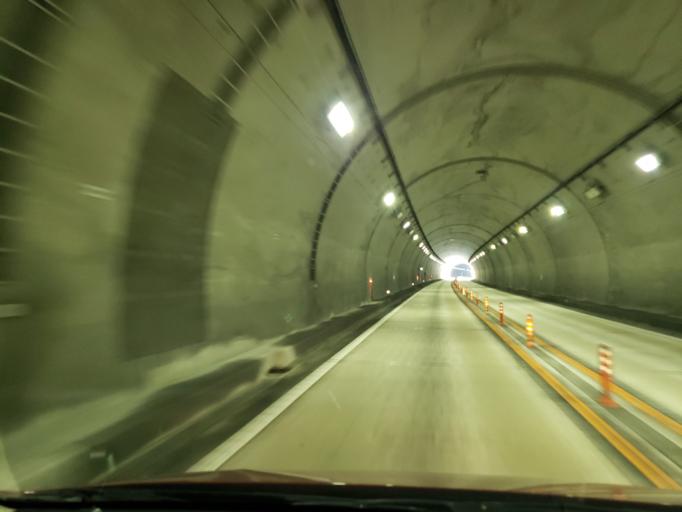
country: JP
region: Tokushima
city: Kamojimacho-jogejima
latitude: 34.1097
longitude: 134.3169
